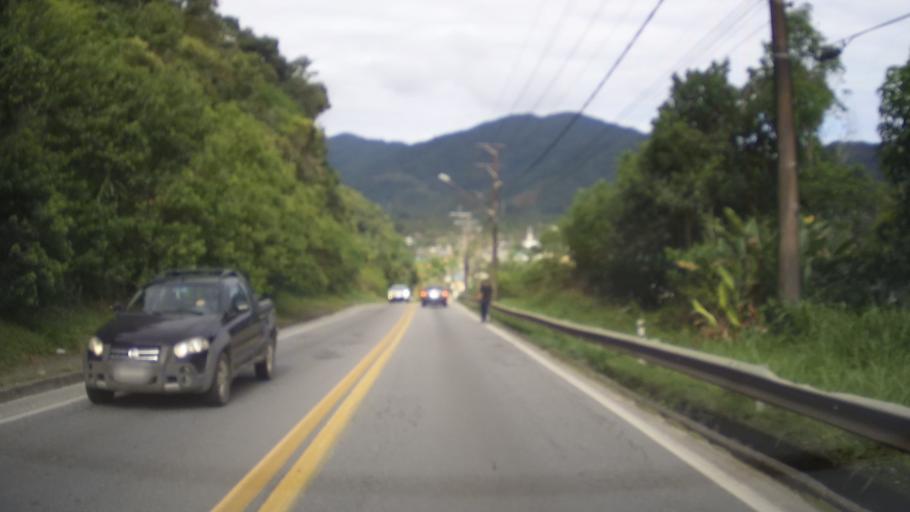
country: BR
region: Sao Paulo
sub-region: Sao Sebastiao
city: Sao Sebastiao
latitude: -23.7827
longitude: -45.6376
